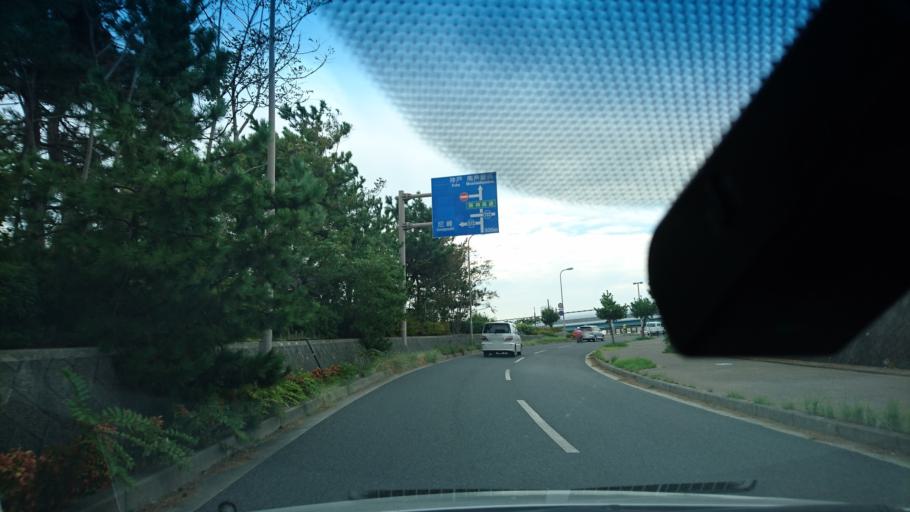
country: JP
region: Hyogo
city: Ashiya
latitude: 34.7160
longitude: 135.3081
